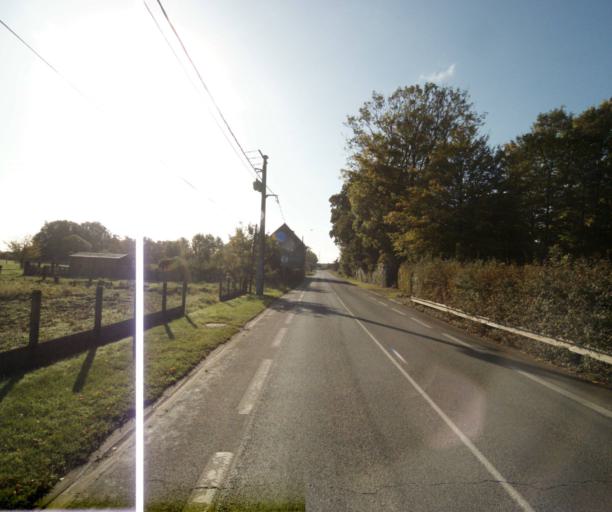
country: FR
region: Nord-Pas-de-Calais
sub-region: Departement du Nord
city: Verlinghem
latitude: 50.6728
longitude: 3.0028
